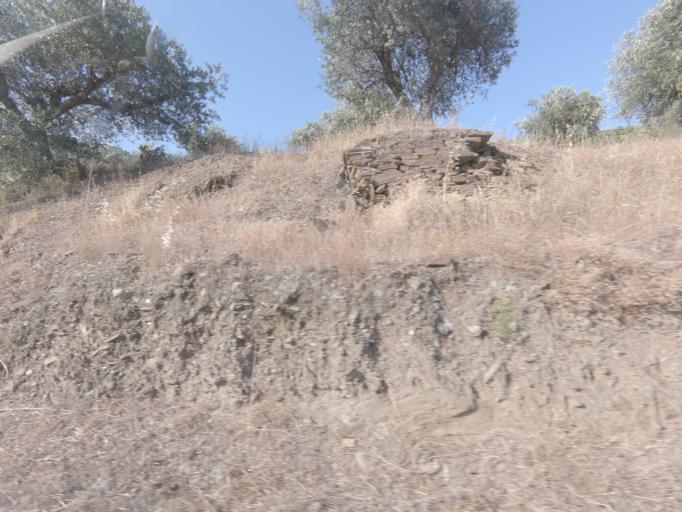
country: PT
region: Viseu
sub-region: Tabuaco
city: Tabuaco
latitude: 41.1751
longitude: -7.5664
